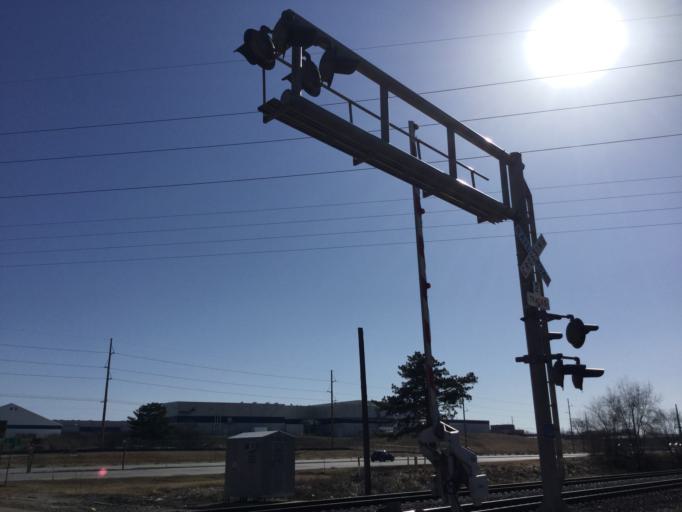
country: US
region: Kansas
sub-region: Sedgwick County
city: Derby
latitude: 37.6165
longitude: -97.2941
